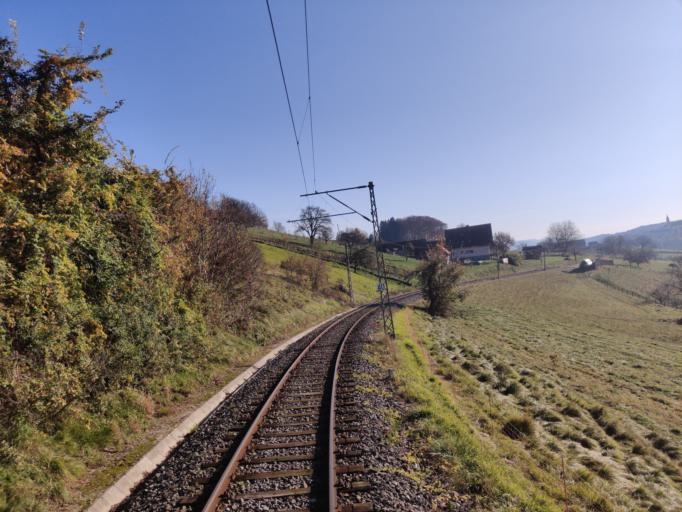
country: AT
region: Styria
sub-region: Politischer Bezirk Suedoststeiermark
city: Trautmannsdorf in Oststeiermark
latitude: 46.8853
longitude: 15.8821
